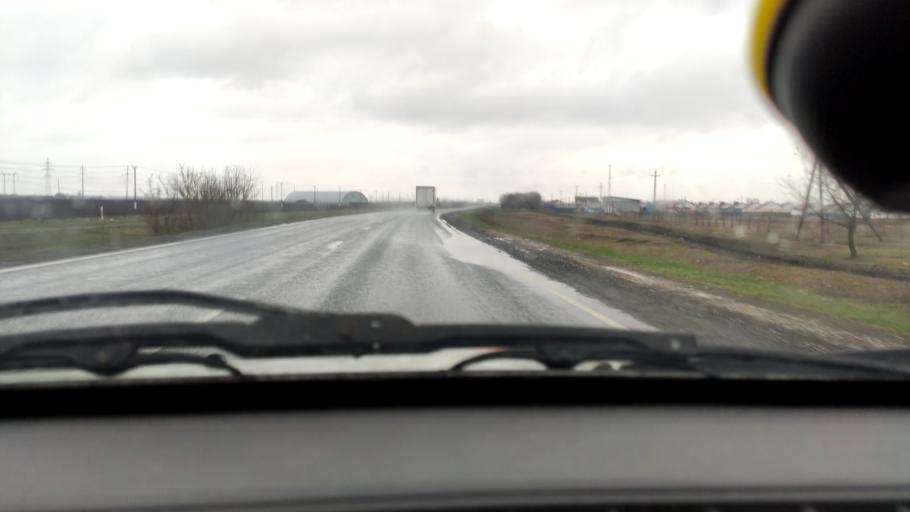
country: RU
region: Samara
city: Povolzhskiy
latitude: 53.6418
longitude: 49.6630
